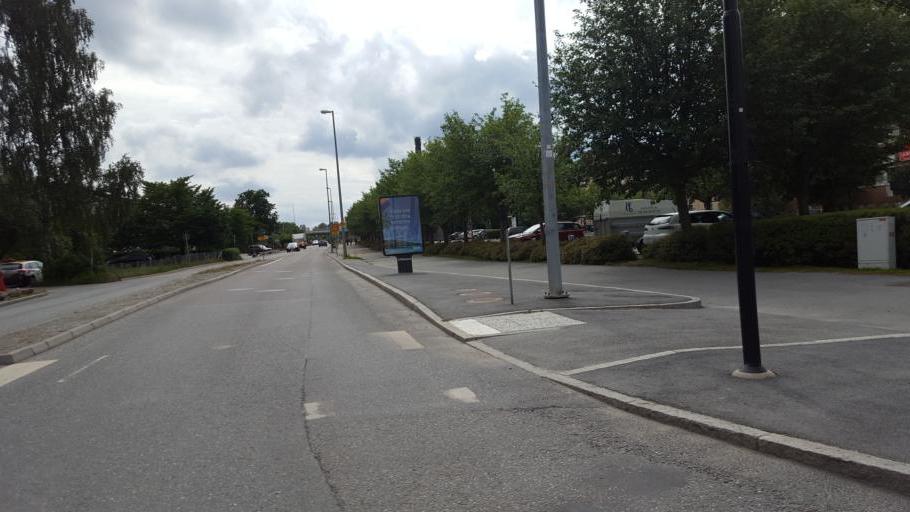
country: SE
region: Stockholm
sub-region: Upplands Vasby Kommun
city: Upplands Vaesby
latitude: 59.5179
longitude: 17.9012
